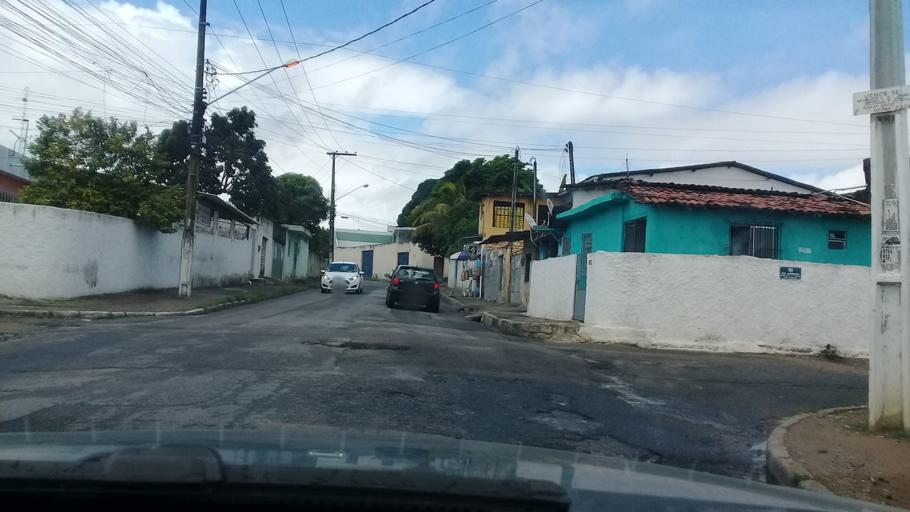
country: BR
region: Pernambuco
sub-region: Jaboatao Dos Guararapes
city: Jaboatao dos Guararapes
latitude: -8.1059
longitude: -34.9636
